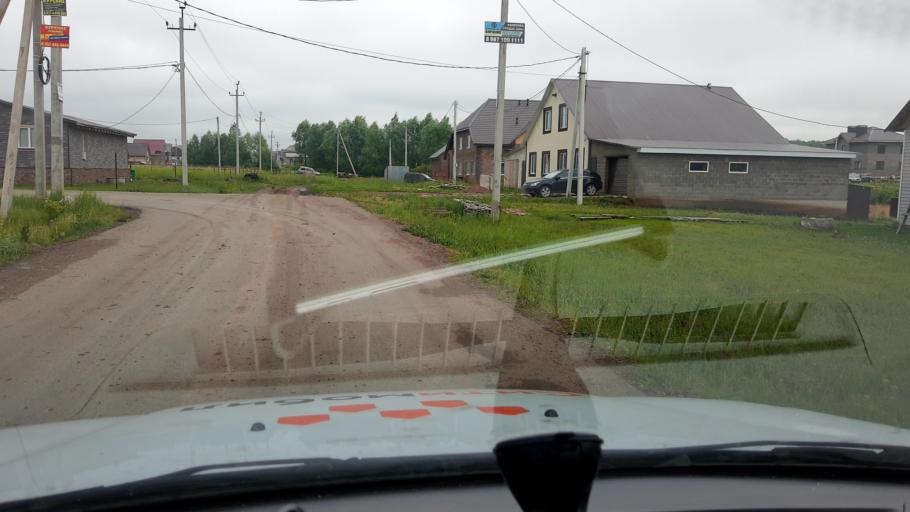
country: RU
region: Bashkortostan
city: Kabakovo
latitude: 54.6496
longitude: 56.2194
